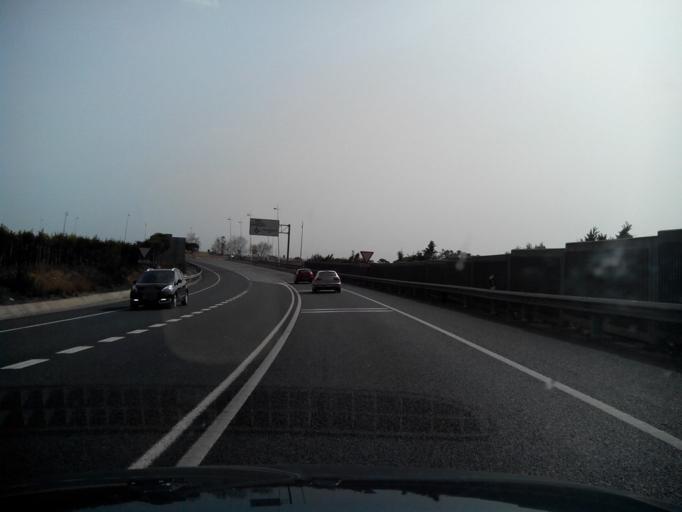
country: ES
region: Catalonia
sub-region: Provincia de Tarragona
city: Creixell
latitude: 41.1570
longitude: 1.4251
